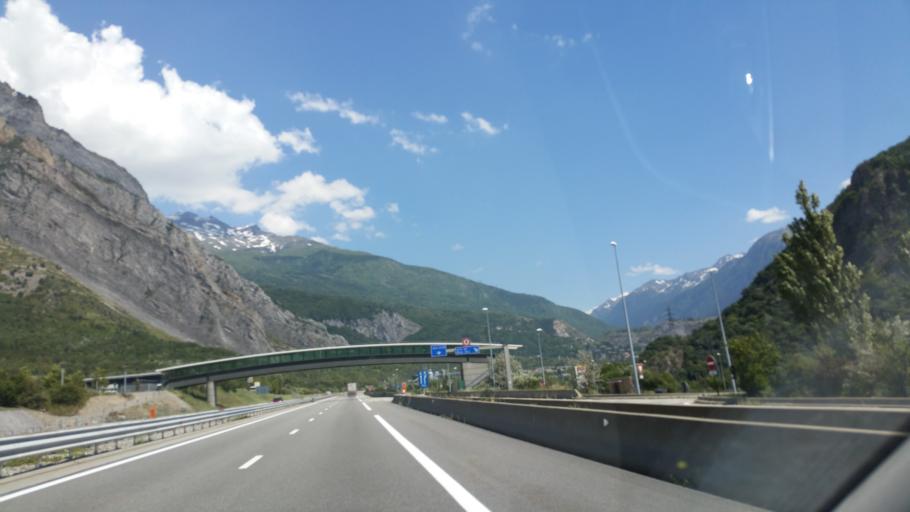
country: FR
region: Rhone-Alpes
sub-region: Departement de la Savoie
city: Villargondran
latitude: 45.2457
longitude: 6.4211
